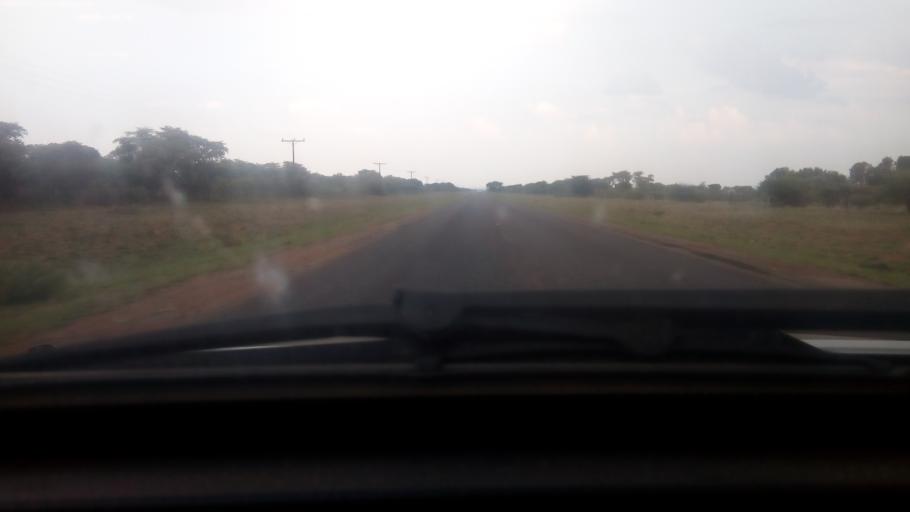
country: BW
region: Kweneng
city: Metsemotlhaba
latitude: -24.4845
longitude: 25.7354
